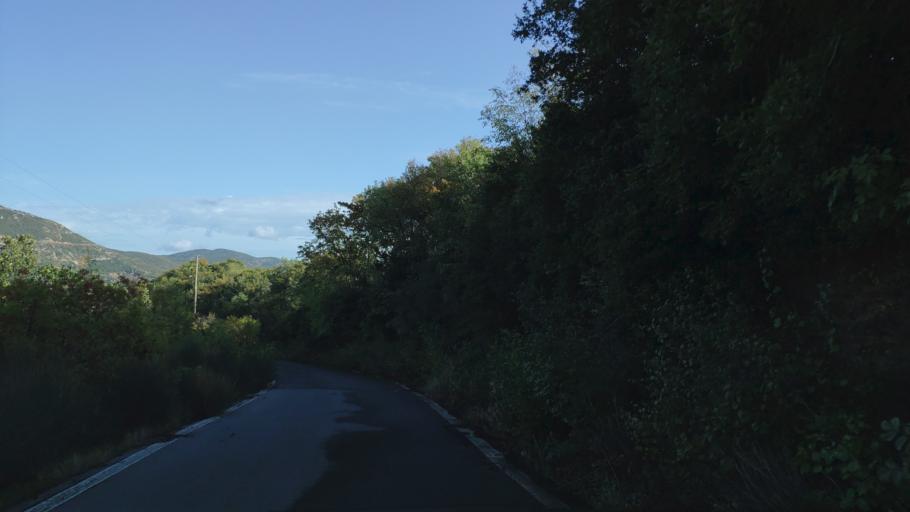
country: GR
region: Peloponnese
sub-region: Nomos Arkadias
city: Dimitsana
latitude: 37.5596
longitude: 22.0356
